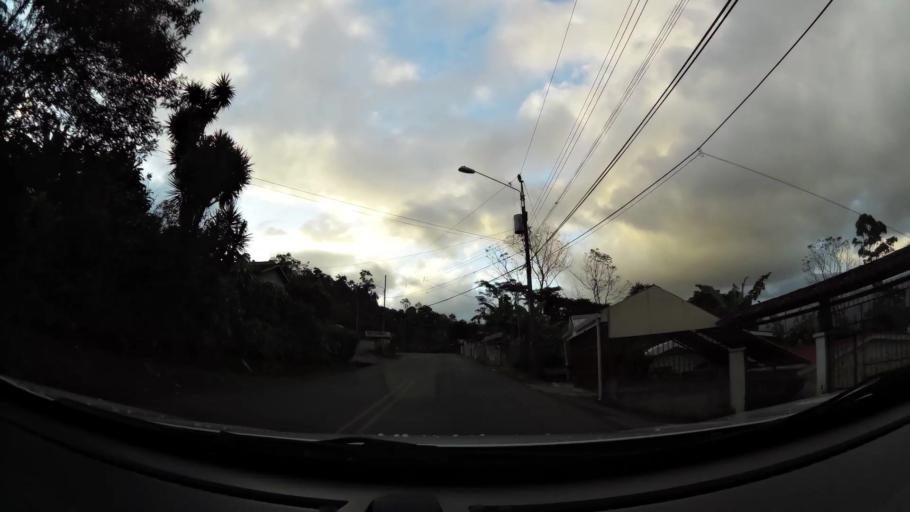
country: CR
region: Cartago
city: Turrialba
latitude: 9.8978
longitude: -83.6902
